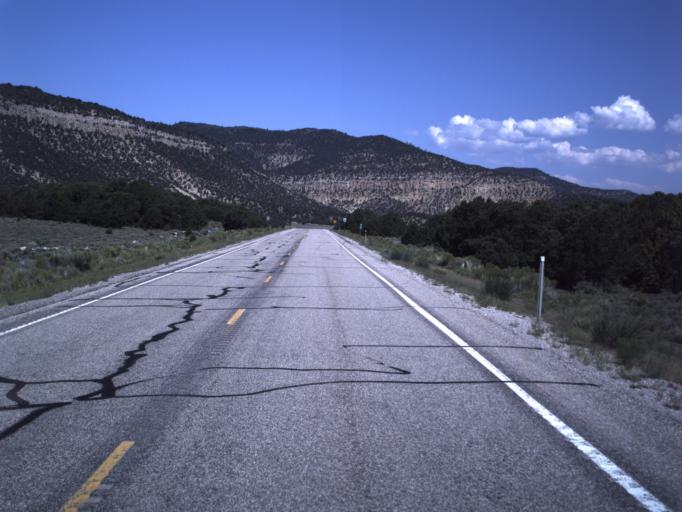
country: US
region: Utah
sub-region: Wayne County
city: Loa
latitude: 38.6990
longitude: -111.3978
